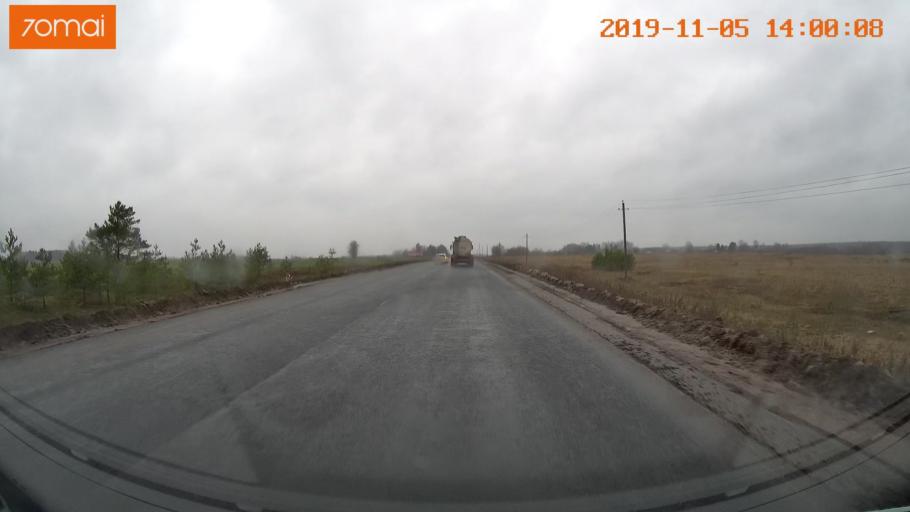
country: RU
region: Ivanovo
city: Kitovo
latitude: 57.0147
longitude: 41.2541
